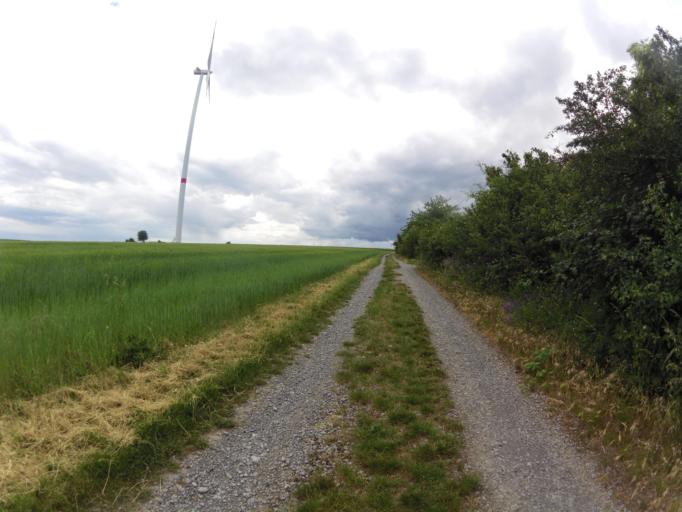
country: DE
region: Bavaria
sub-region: Regierungsbezirk Unterfranken
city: Thungersheim
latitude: 49.8822
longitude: 9.8776
